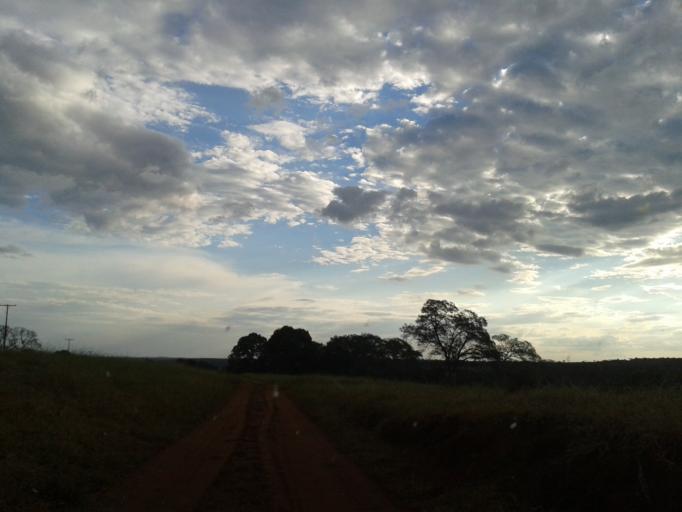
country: BR
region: Minas Gerais
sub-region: Campina Verde
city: Campina Verde
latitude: -19.3380
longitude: -49.6506
